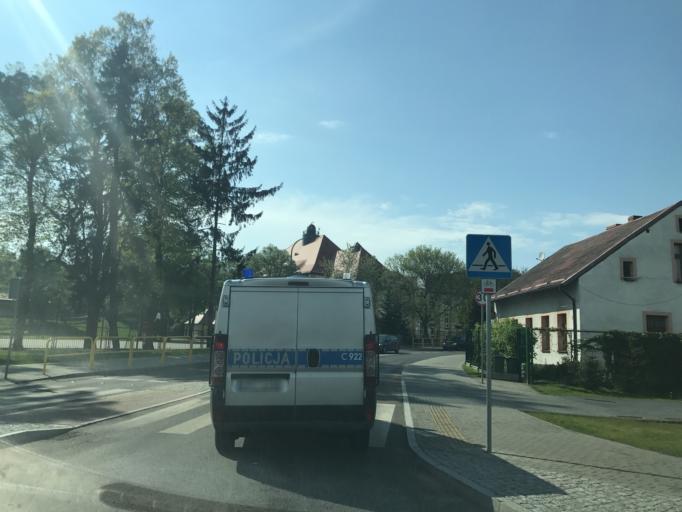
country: PL
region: Kujawsko-Pomorskie
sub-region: Powiat swiecki
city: Swiecie
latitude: 53.4105
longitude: 18.4464
